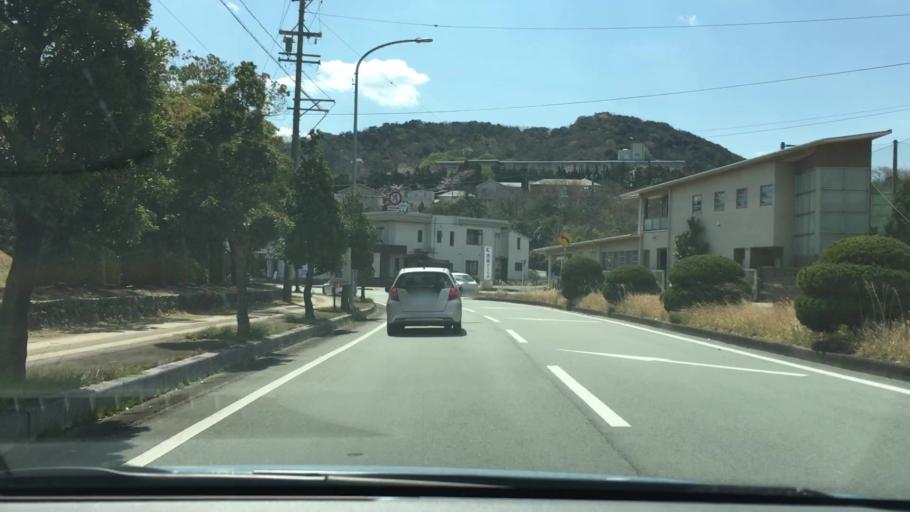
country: JP
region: Mie
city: Toba
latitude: 34.4682
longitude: 136.8490
